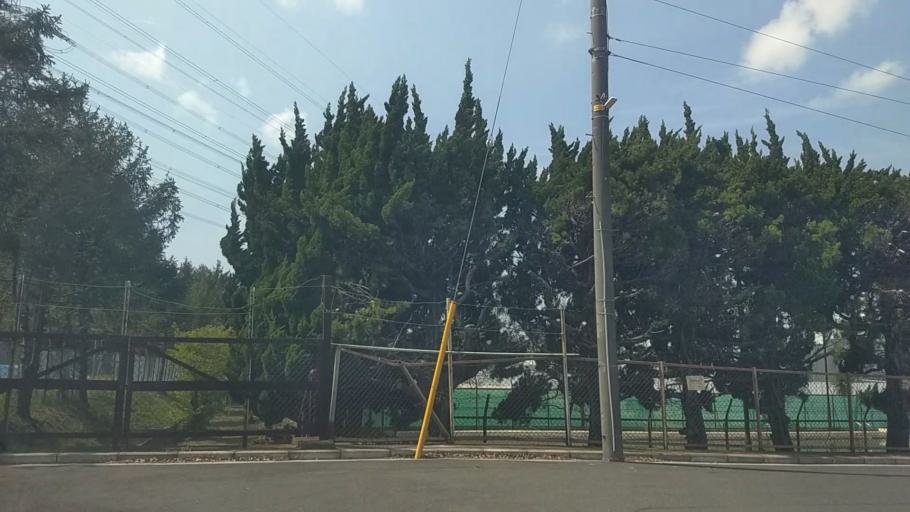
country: JP
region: Kanagawa
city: Kamakura
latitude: 35.3700
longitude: 139.5751
